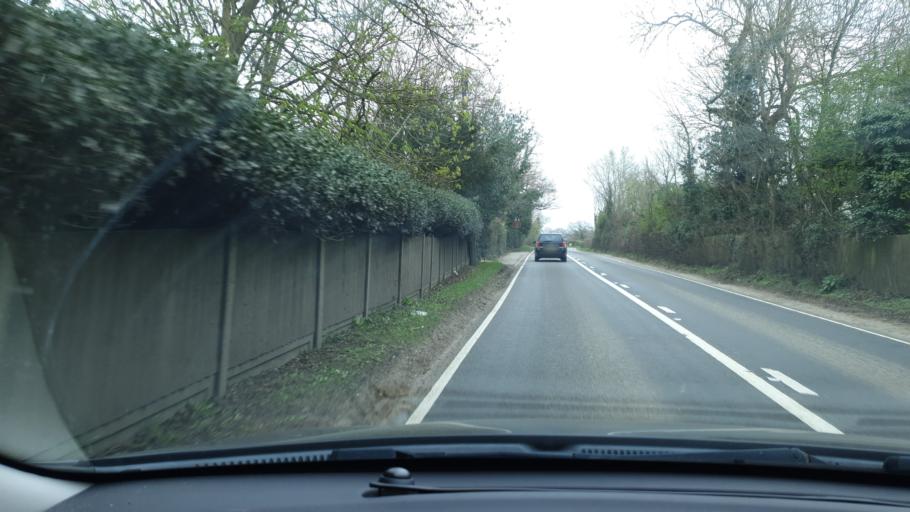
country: GB
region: England
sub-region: Essex
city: Great Horkesley
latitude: 51.9482
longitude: 0.8751
